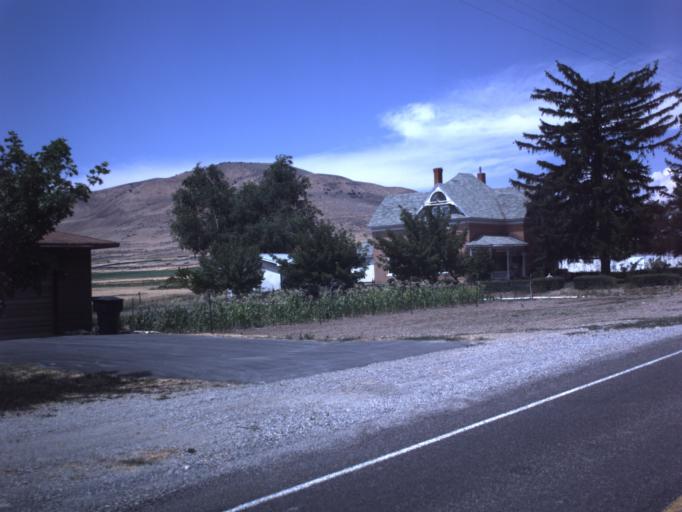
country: US
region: Utah
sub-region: Box Elder County
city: Tremonton
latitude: 41.6530
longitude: -112.2958
